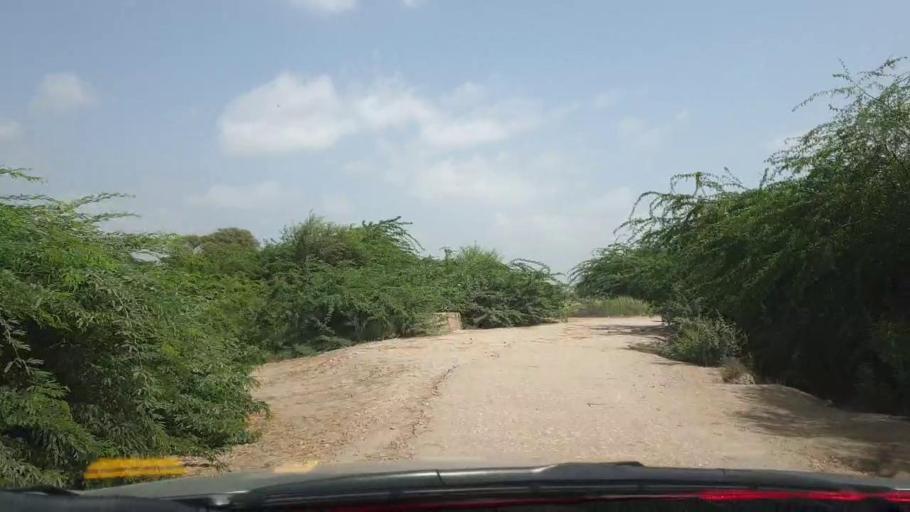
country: PK
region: Sindh
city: Talhar
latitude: 24.8837
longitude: 68.8289
